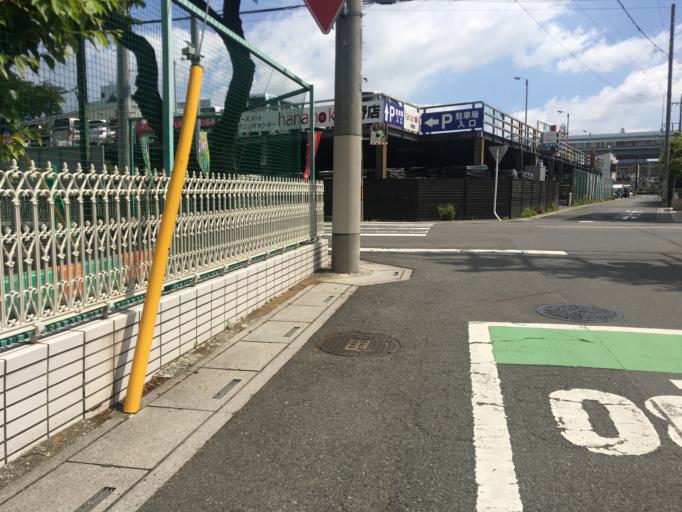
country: JP
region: Saitama
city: Yono
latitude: 35.8847
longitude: 139.6131
